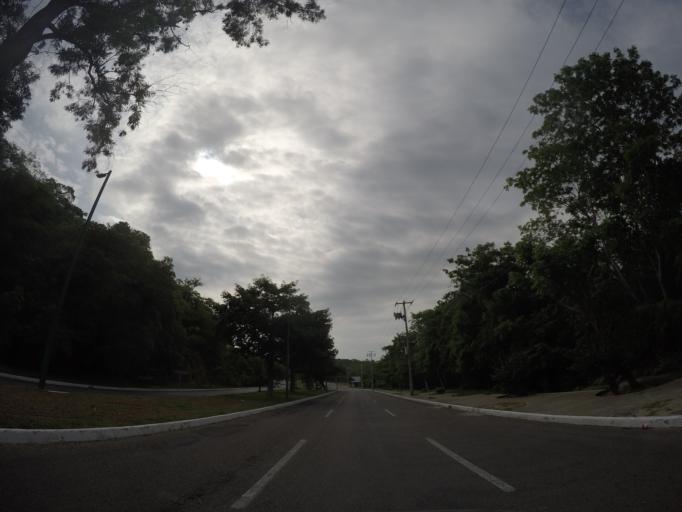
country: MX
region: Oaxaca
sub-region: Santa Maria Huatulco
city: Sector H Tres
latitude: 15.7809
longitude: -96.1548
